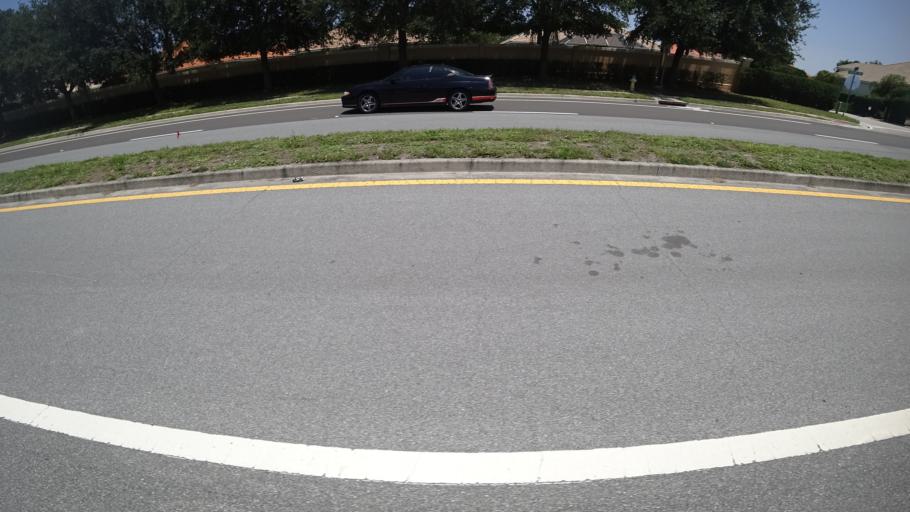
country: US
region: Florida
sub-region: Manatee County
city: Samoset
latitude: 27.4288
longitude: -82.5030
